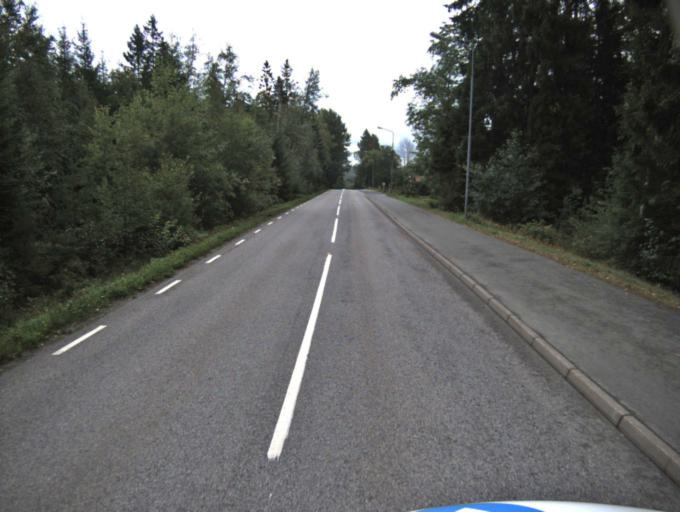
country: SE
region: Vaestra Goetaland
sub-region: Ulricehamns Kommun
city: Ulricehamn
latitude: 57.7727
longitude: 13.4372
